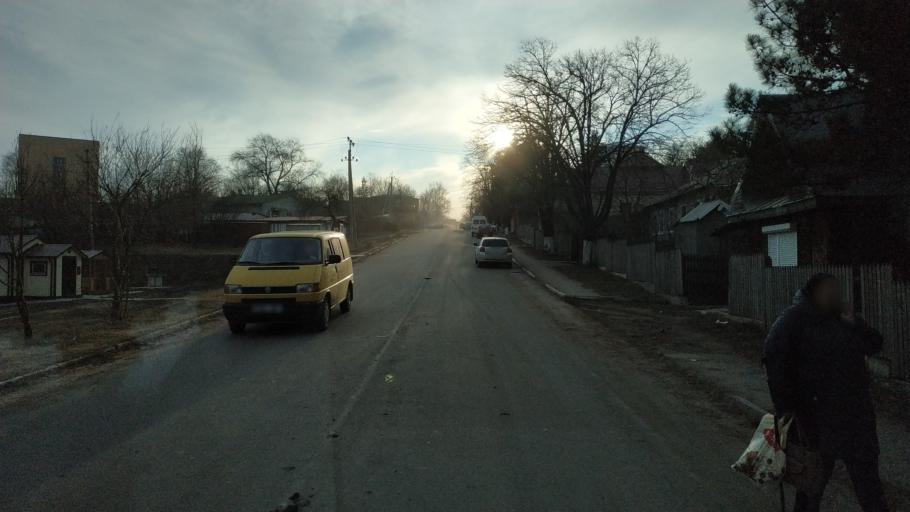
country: MD
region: Nisporeni
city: Nisporeni
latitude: 47.0888
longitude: 28.1785
